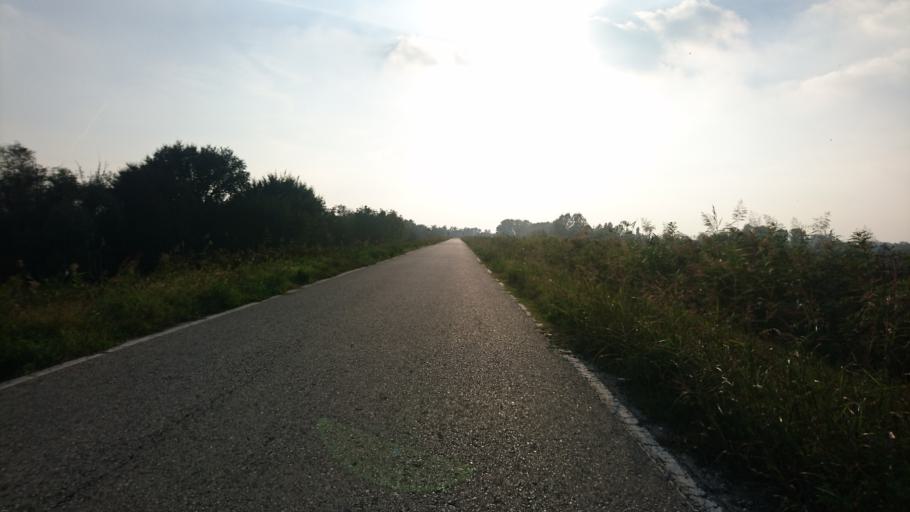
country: IT
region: Veneto
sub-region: Provincia di Rovigo
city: Canaro
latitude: 44.9224
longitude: 11.6961
